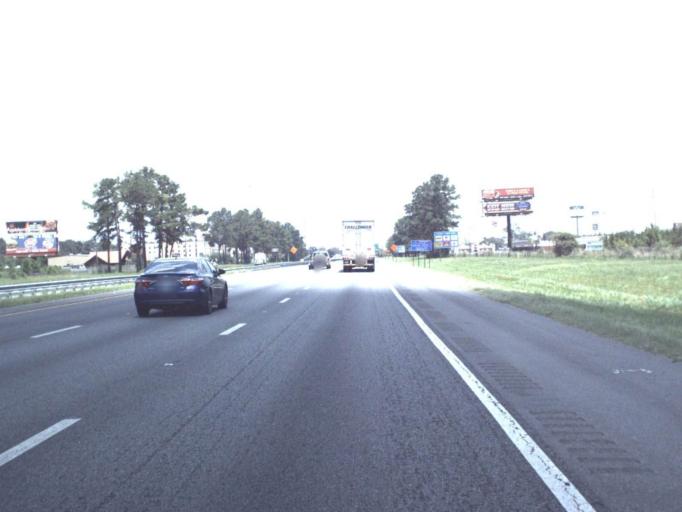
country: US
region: Florida
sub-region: Columbia County
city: Lake City
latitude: 30.1708
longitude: -82.6838
